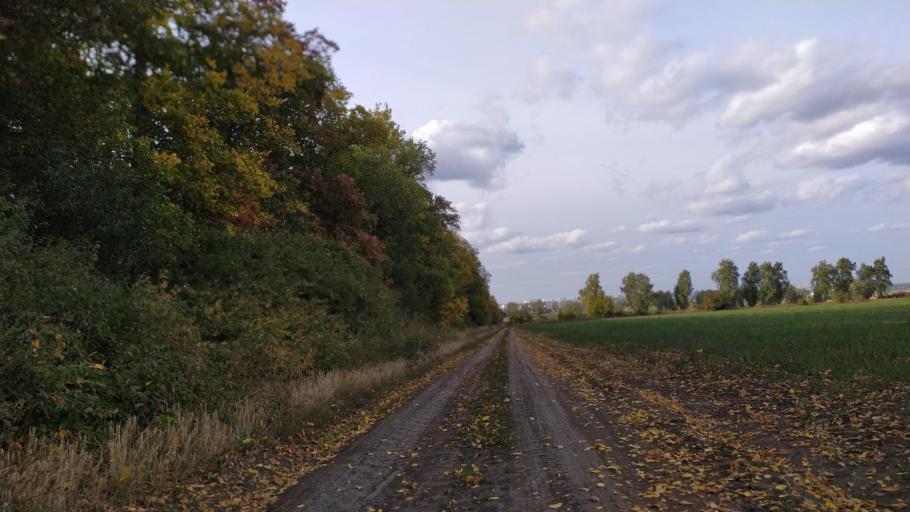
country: RU
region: Kursk
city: Kursk
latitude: 51.6195
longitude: 36.1630
